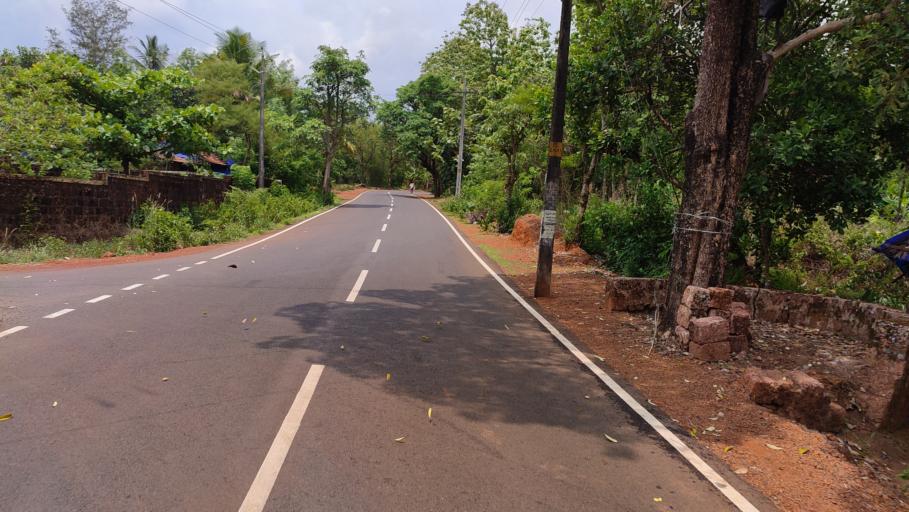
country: IN
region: Kerala
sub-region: Kasaragod District
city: Kannangad
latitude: 12.3228
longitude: 75.1267
